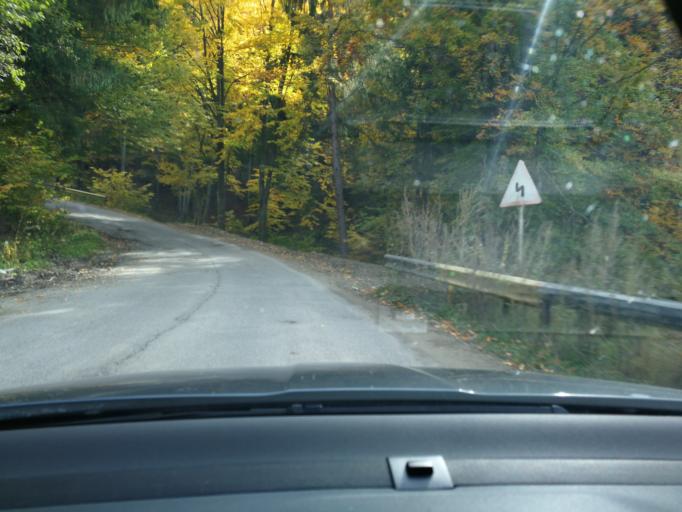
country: RO
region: Prahova
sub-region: Comuna Brebu
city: Pietriceaua
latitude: 45.2055
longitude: 25.7977
